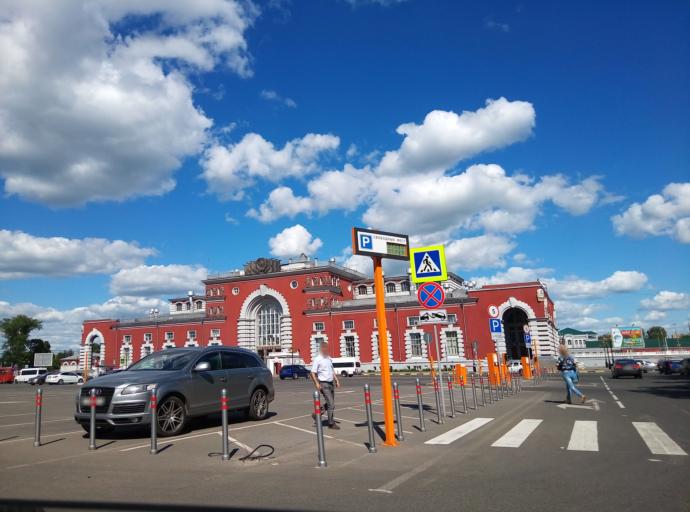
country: RU
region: Kursk
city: Kursk
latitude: 51.7495
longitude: 36.2261
